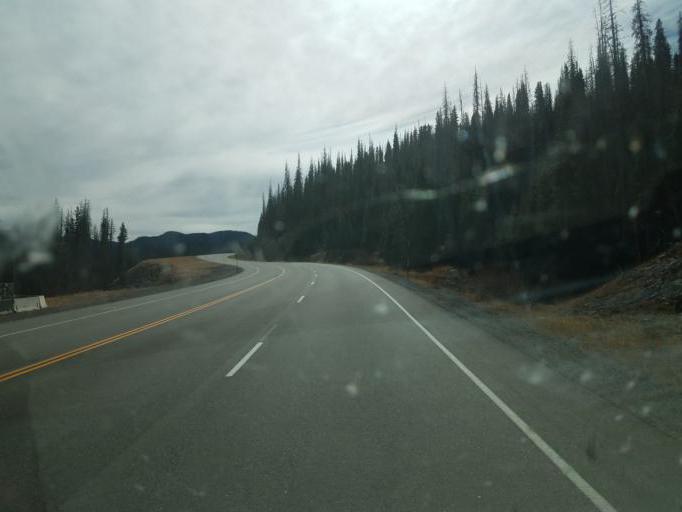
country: US
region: Colorado
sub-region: Archuleta County
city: Pagosa Springs
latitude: 37.5003
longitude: -106.7705
